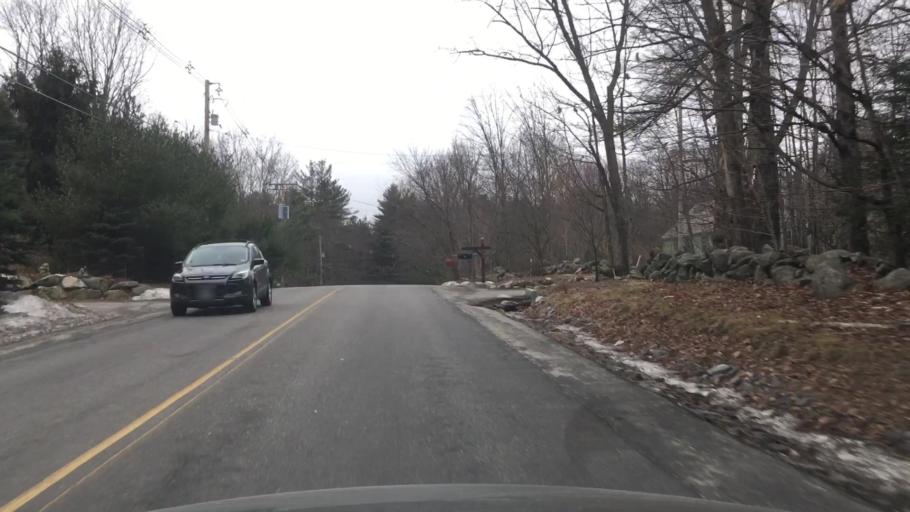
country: US
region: New Hampshire
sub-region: Hillsborough County
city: Goffstown
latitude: 42.9718
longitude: -71.6344
